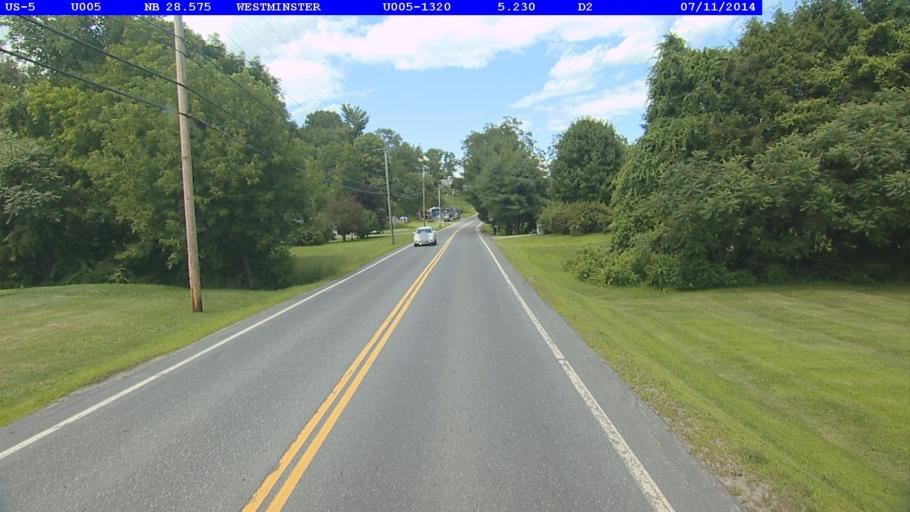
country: US
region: Vermont
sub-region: Windham County
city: Bellows Falls
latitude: 43.0868
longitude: -72.4391
